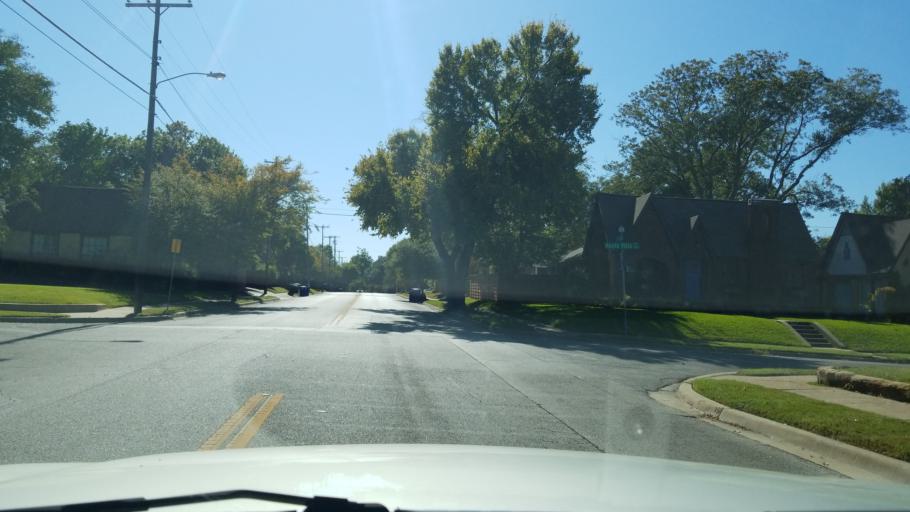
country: US
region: Texas
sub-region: Dallas County
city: Highland Park
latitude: 32.8046
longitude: -96.7417
